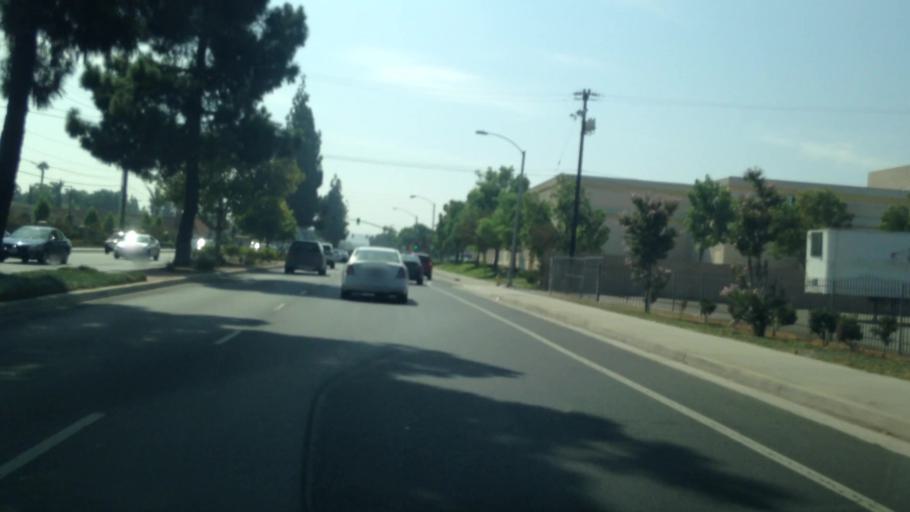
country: US
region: California
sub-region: Riverside County
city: Pedley
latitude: 33.9287
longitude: -117.4536
